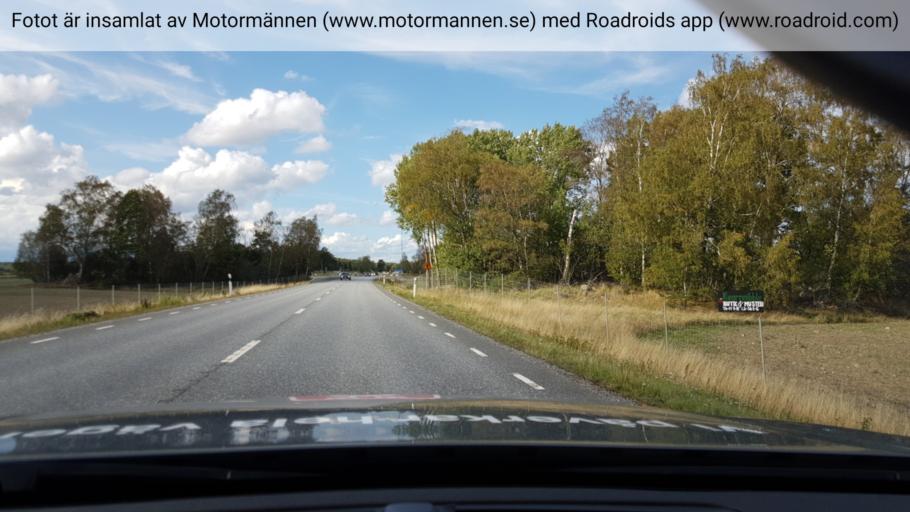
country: SE
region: Stockholm
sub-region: Upplands-Bro Kommun
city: Bro
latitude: 59.5937
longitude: 17.6168
